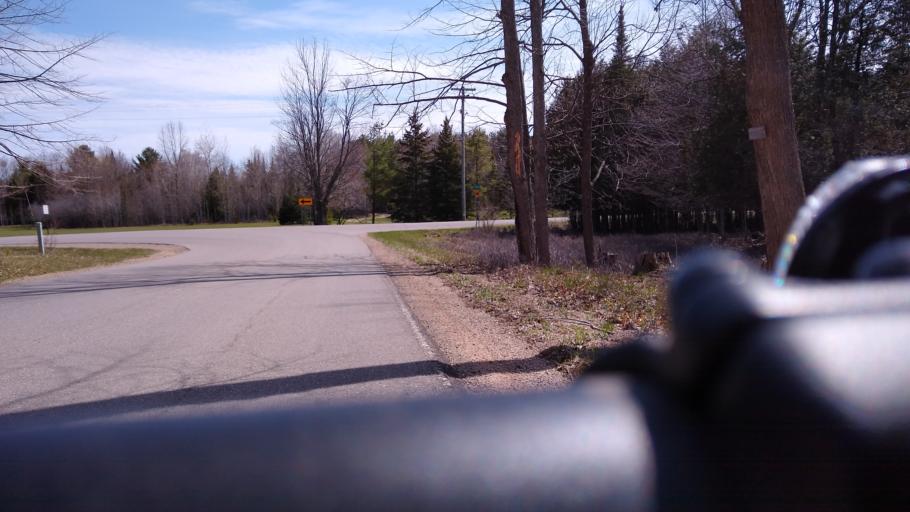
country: US
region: Michigan
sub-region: Delta County
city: Escanaba
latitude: 45.6961
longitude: -87.1629
